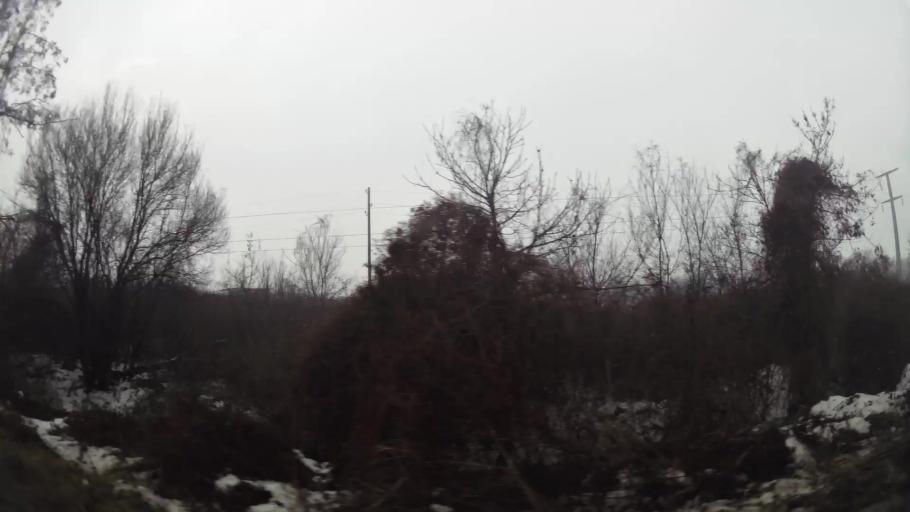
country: MK
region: Ilinden
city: Idrizovo
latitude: 41.9486
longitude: 21.5905
